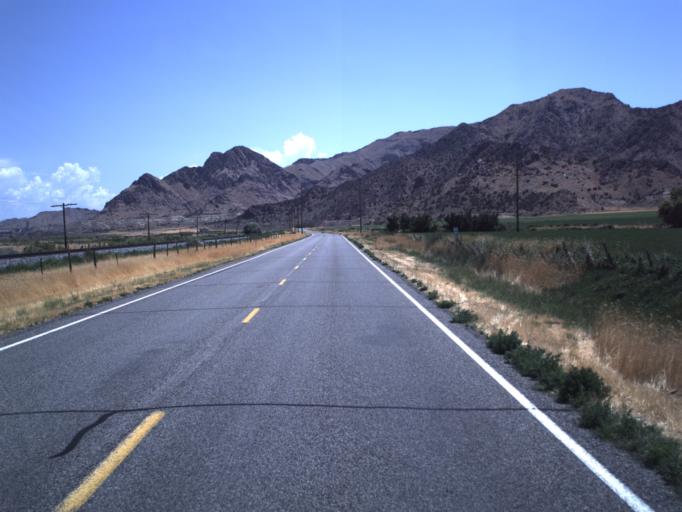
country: US
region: Utah
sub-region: Millard County
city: Delta
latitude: 39.5374
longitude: -112.2621
